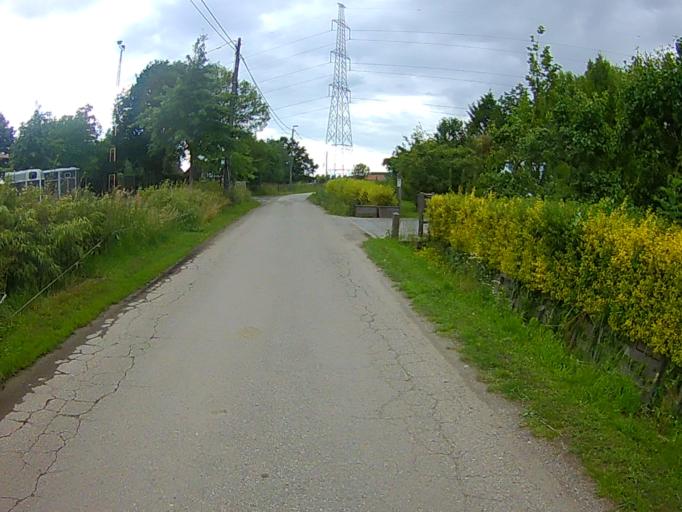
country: BE
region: Flanders
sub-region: Provincie Antwerpen
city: Ranst
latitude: 51.1625
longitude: 4.5540
